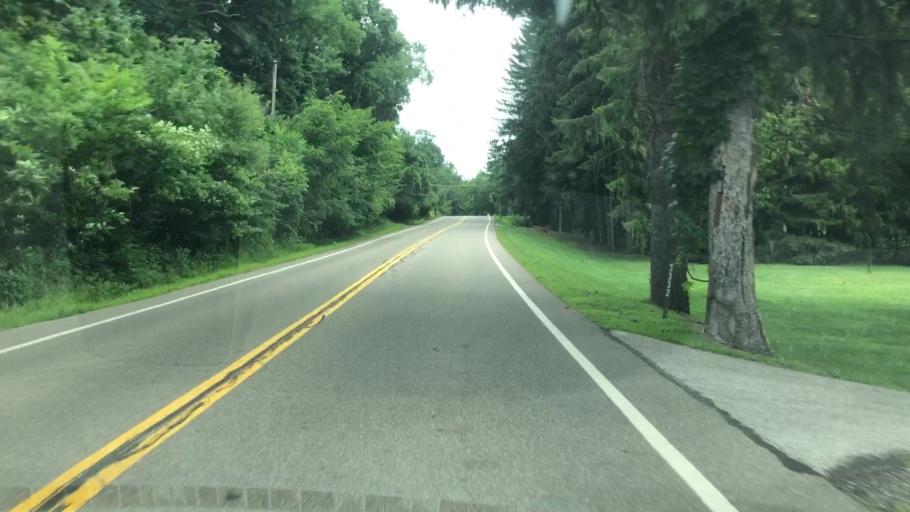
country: US
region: Ohio
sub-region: Summit County
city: Montrose-Ghent
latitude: 41.1571
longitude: -81.6244
